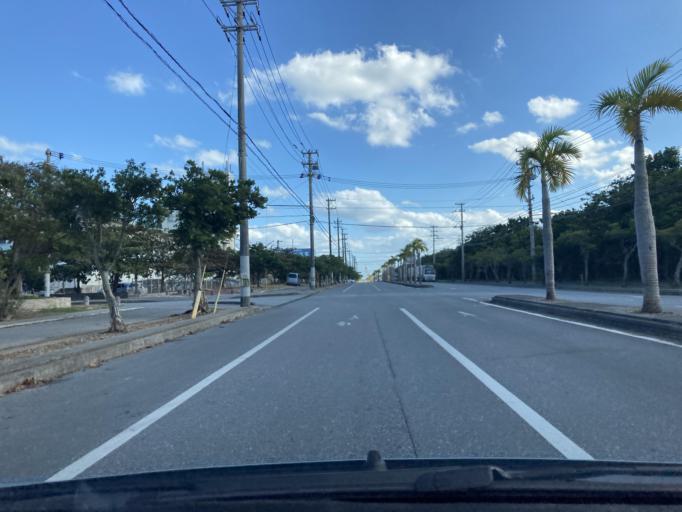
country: JP
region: Okinawa
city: Katsuren-haebaru
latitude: 26.3345
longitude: 127.8507
